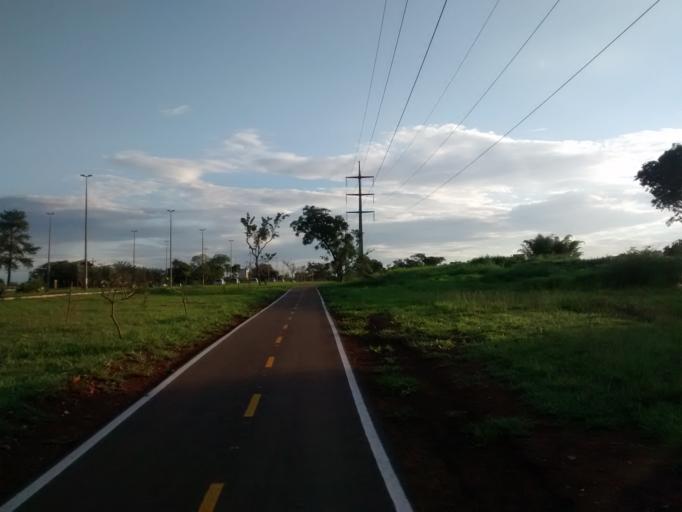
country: BR
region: Federal District
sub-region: Brasilia
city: Brasilia
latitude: -15.7682
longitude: -47.8636
